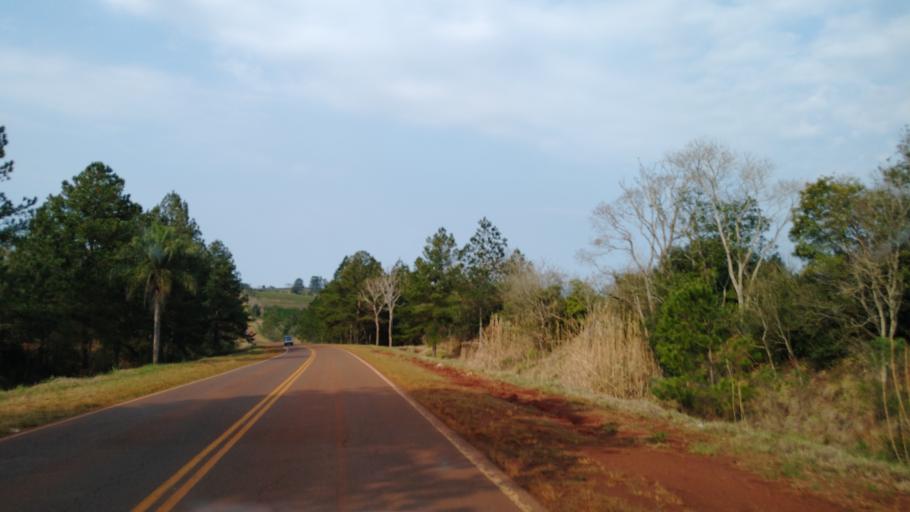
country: AR
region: Misiones
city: Campo Viera
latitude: -27.3150
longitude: -55.1061
